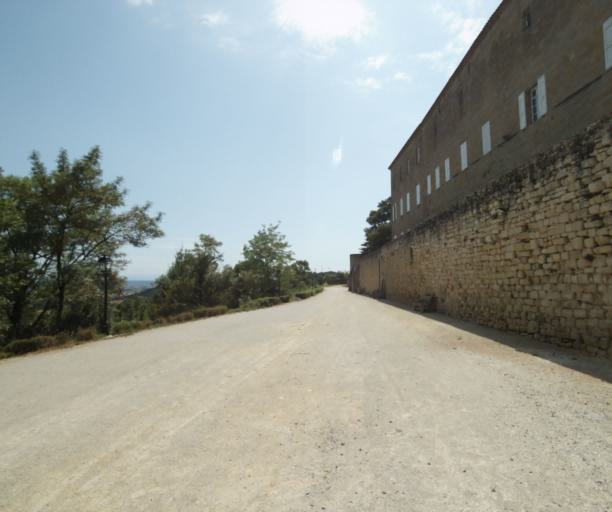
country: FR
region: Midi-Pyrenees
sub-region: Departement de la Haute-Garonne
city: Saint-Felix-Lauragais
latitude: 43.4487
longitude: 1.8902
